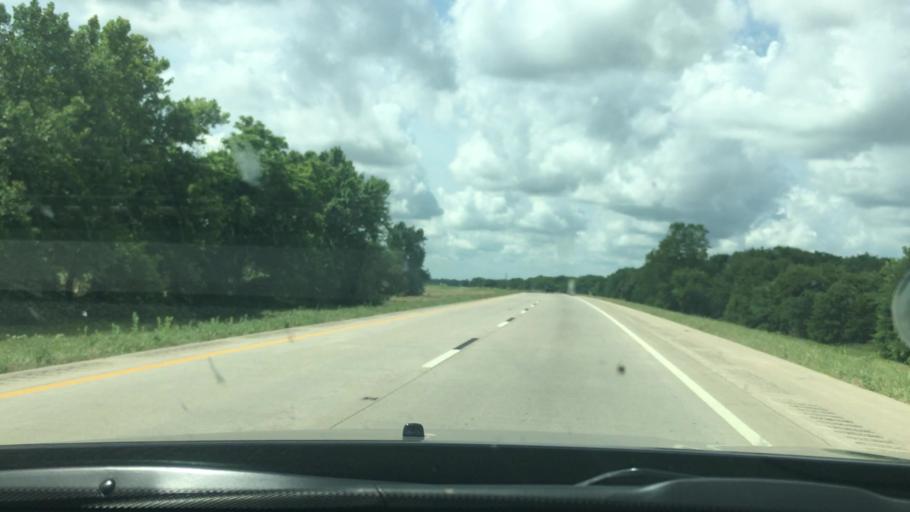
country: US
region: Oklahoma
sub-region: Love County
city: Marietta
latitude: 33.8119
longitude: -97.1341
